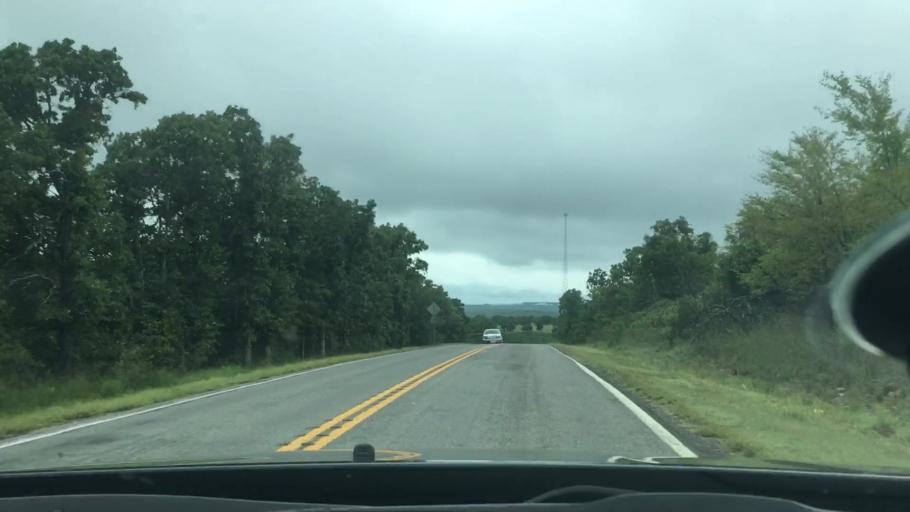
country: US
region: Oklahoma
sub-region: Sequoyah County
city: Vian
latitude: 35.6227
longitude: -94.9606
